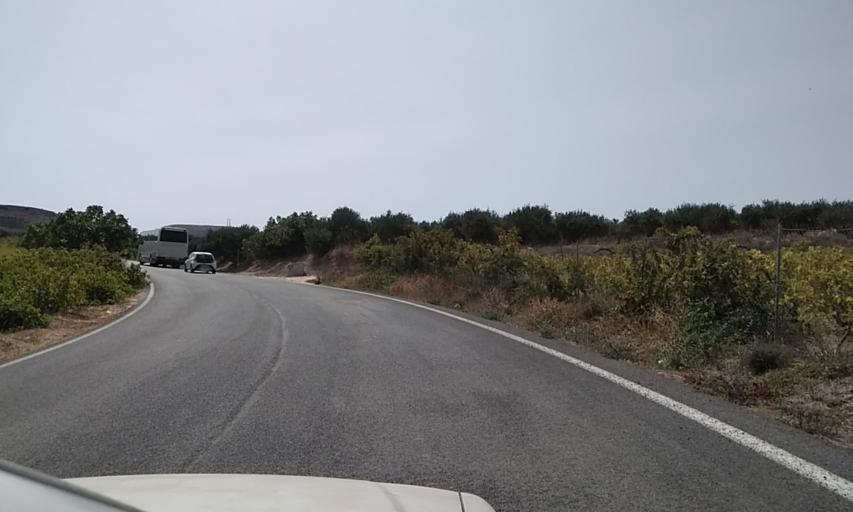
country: GR
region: Crete
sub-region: Nomos Lasithiou
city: Makry-Gialos
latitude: 35.0995
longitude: 26.0592
